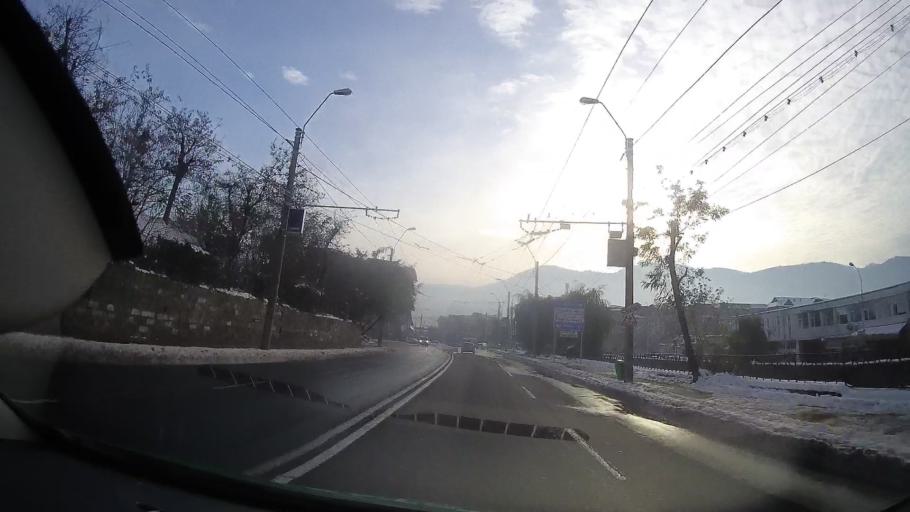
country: RO
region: Neamt
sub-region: Municipiul Piatra-Neamt
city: Valeni
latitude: 46.9278
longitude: 26.3724
